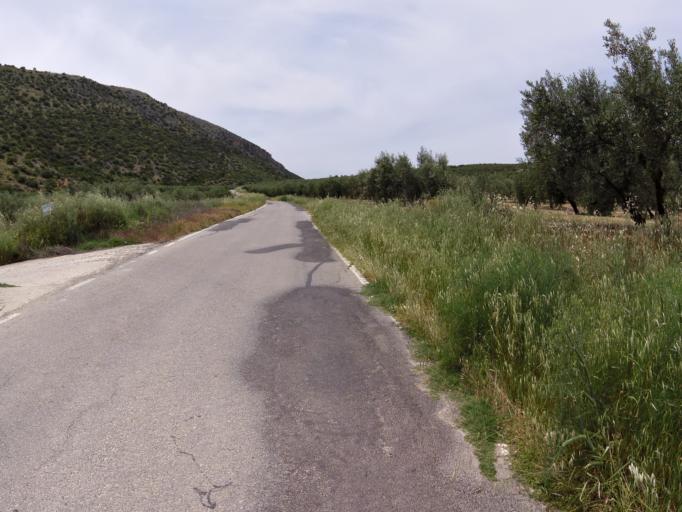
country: ES
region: Andalusia
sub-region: Province of Cordoba
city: Luque
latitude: 37.5194
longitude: -4.2236
